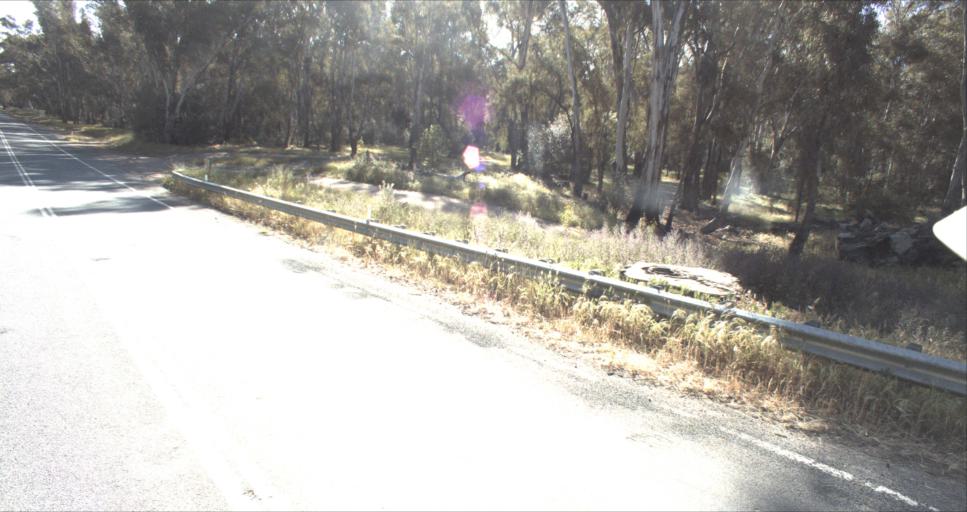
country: AU
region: New South Wales
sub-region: Leeton
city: Leeton
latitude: -34.6395
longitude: 146.3726
